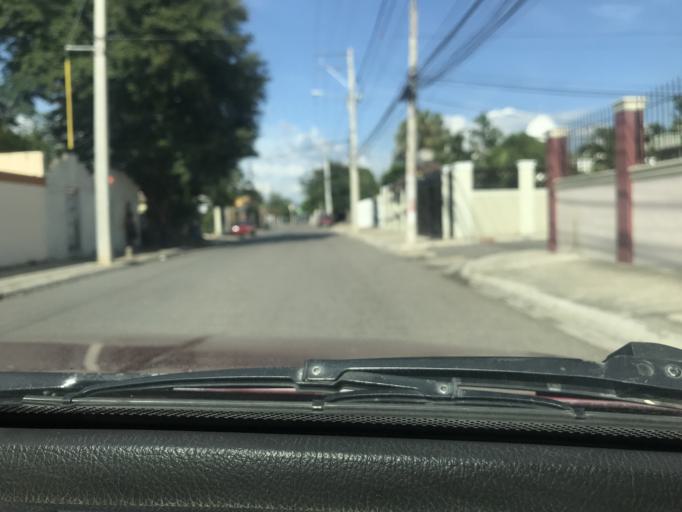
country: DO
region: Santiago
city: Licey al Medio
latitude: 19.4058
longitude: -70.6355
